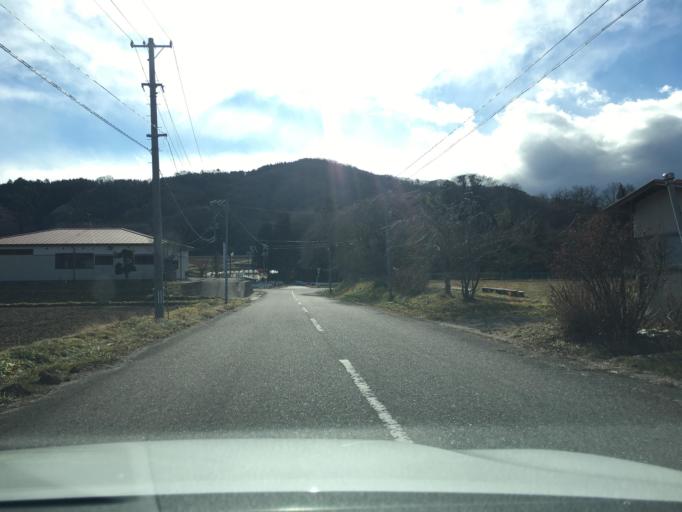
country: JP
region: Fukushima
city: Funehikimachi-funehiki
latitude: 37.3596
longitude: 140.6174
